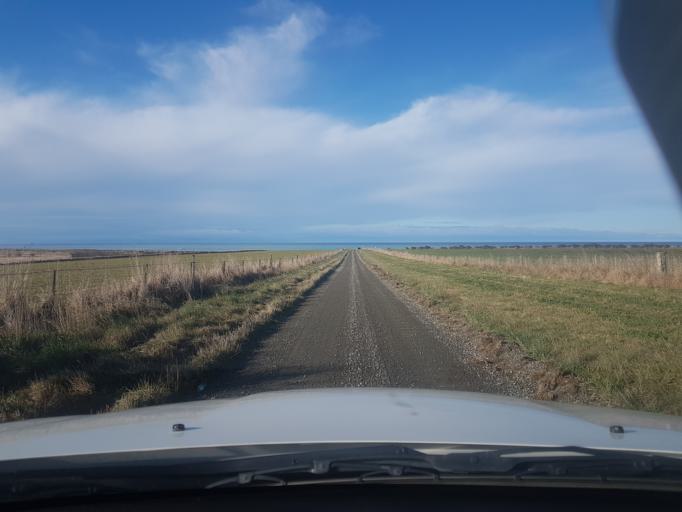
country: NZ
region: Canterbury
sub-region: Timaru District
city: Timaru
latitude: -44.4635
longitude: 171.2388
